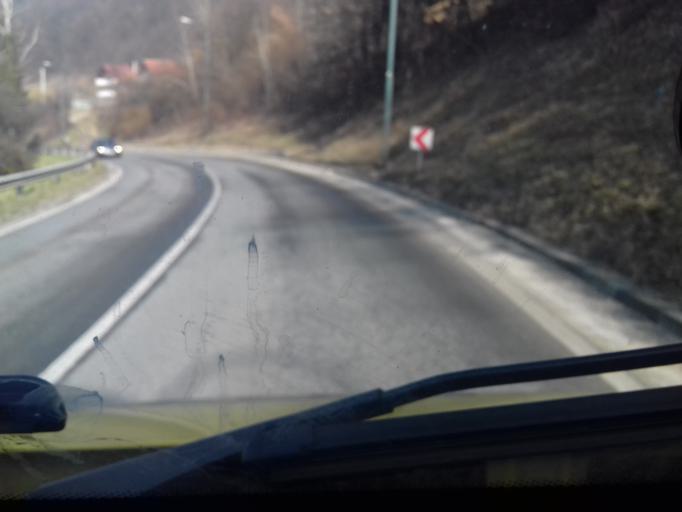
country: BA
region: Federation of Bosnia and Herzegovina
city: Vogosca
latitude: 43.9048
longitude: 18.3288
